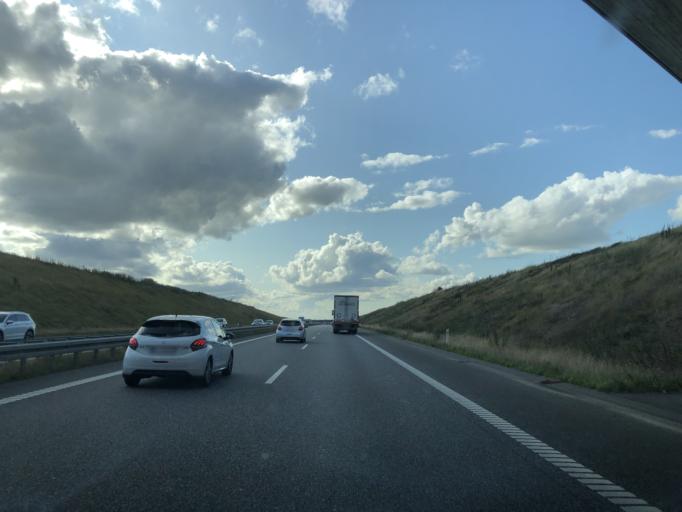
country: DK
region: Central Jutland
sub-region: Skanderborg Kommune
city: Ry
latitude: 56.1465
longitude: 9.7959
